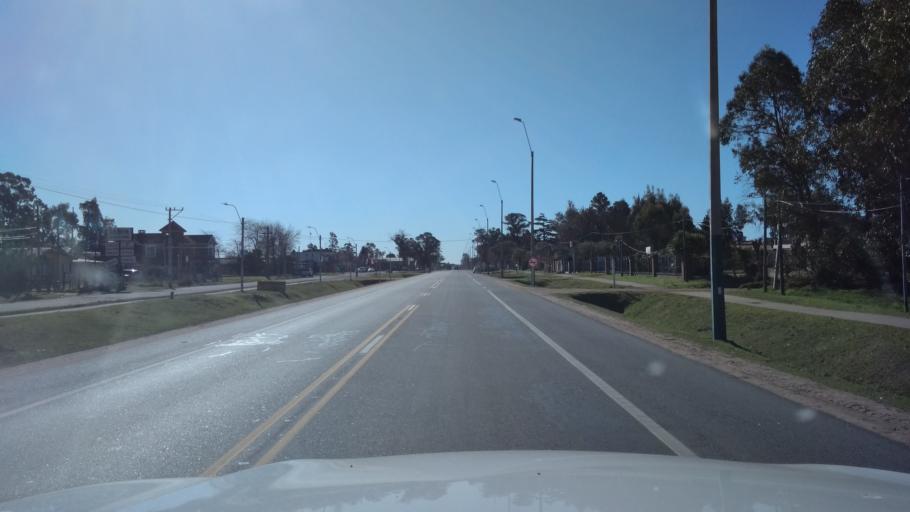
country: UY
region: Canelones
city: Atlantida
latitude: -34.7596
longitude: -55.7659
